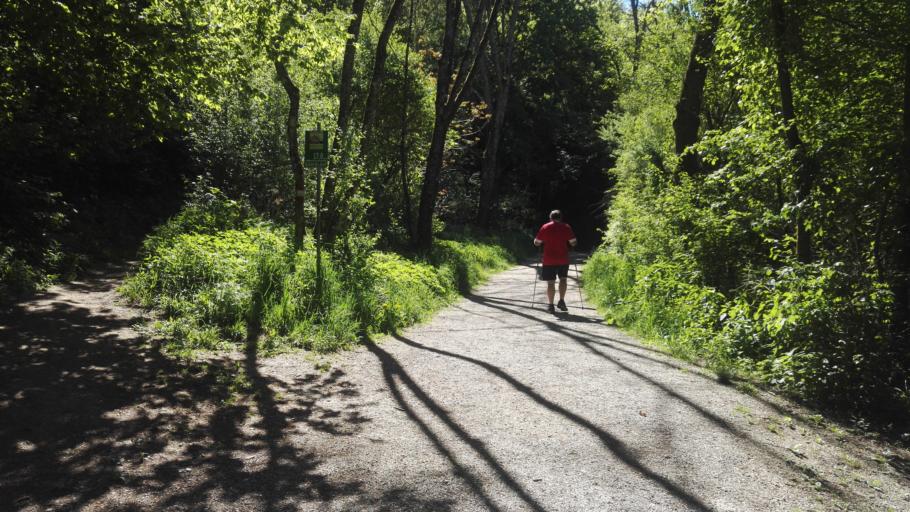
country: AT
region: Styria
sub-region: Politischer Bezirk Graz-Umgebung
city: Thal
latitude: 47.0704
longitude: 15.3678
